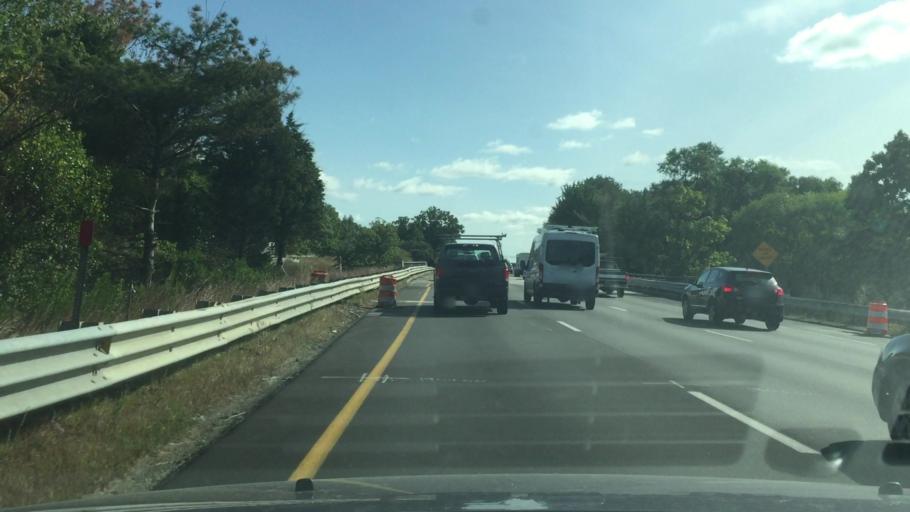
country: US
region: Massachusetts
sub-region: Essex County
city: Lawrence
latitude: 42.6746
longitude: -71.1730
